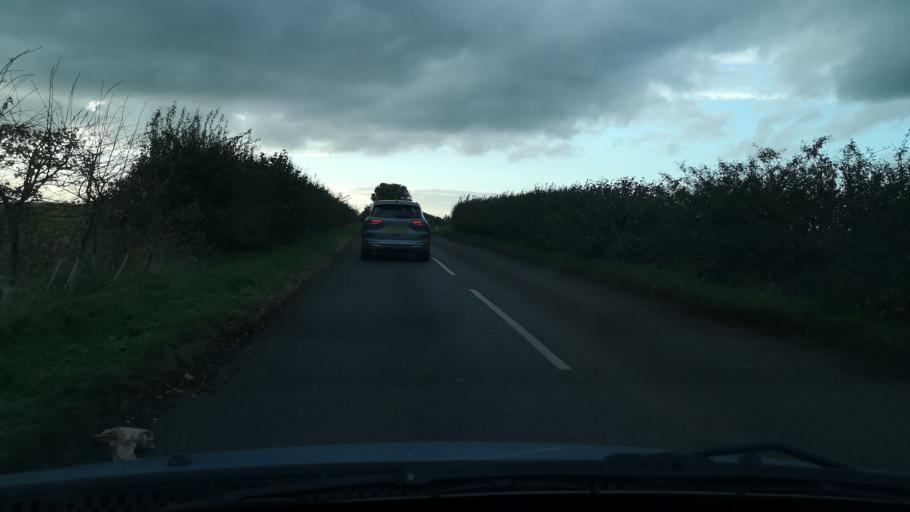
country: GB
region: England
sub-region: Doncaster
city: Norton
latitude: 53.6328
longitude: -1.1959
